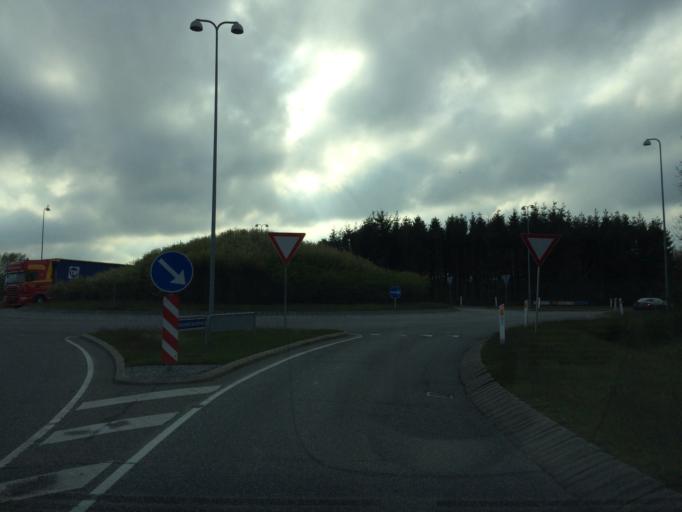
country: DK
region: Central Jutland
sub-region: Herning Kommune
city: Sunds
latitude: 56.3319
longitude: 8.9857
